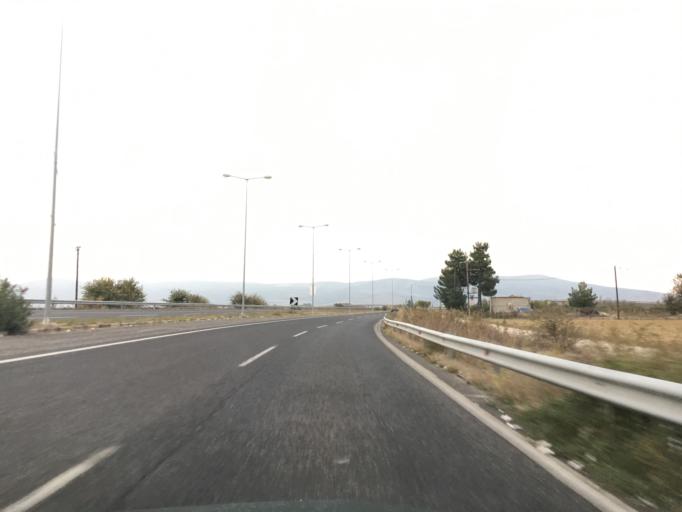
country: GR
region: Thessaly
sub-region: Trikala
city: Trikala
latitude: 39.5650
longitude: 21.8042
